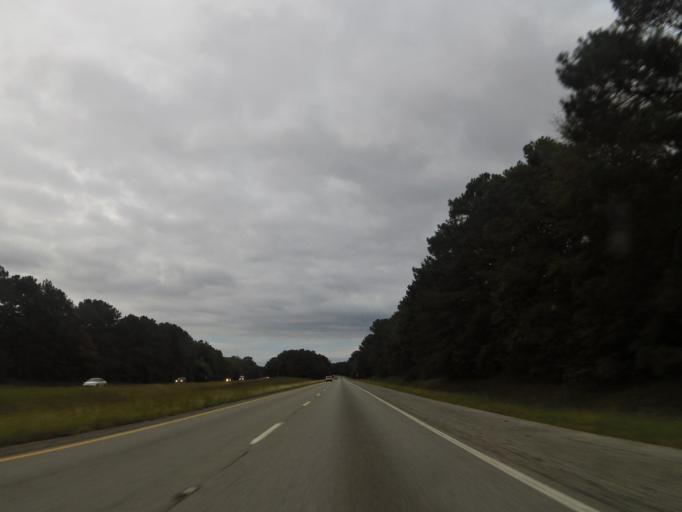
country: US
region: Alabama
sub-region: Saint Clair County
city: Ashville
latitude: 33.8103
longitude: -86.3576
